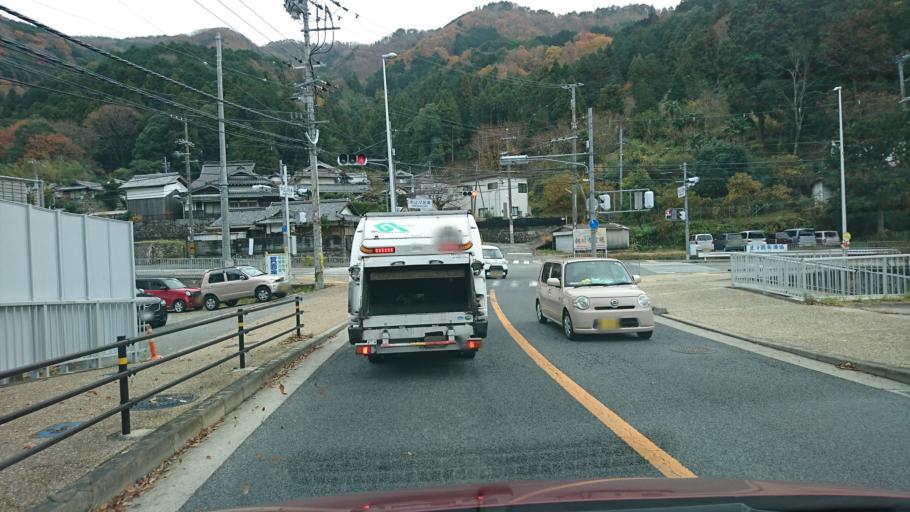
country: JP
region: Osaka
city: Mino
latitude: 34.8854
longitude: 135.4642
